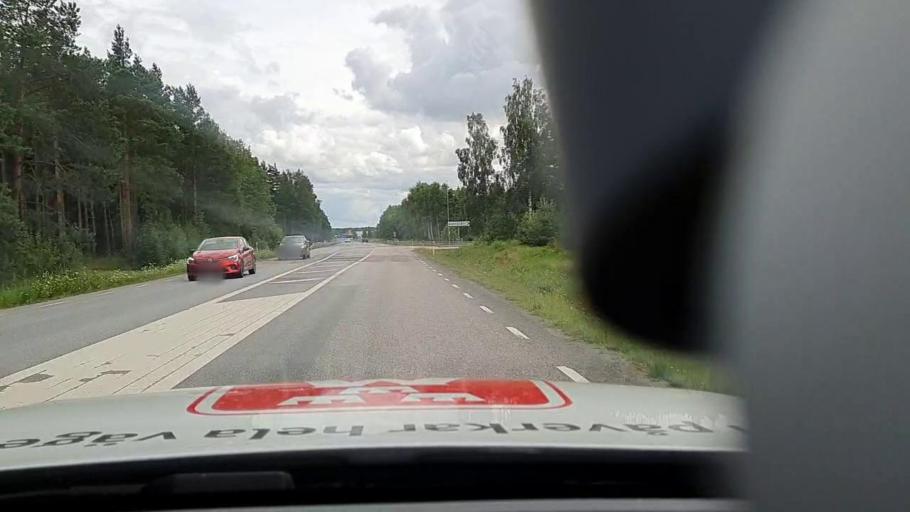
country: SE
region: Vaestra Goetaland
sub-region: Lidkopings Kommun
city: Lidkoping
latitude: 58.5113
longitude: 13.1178
